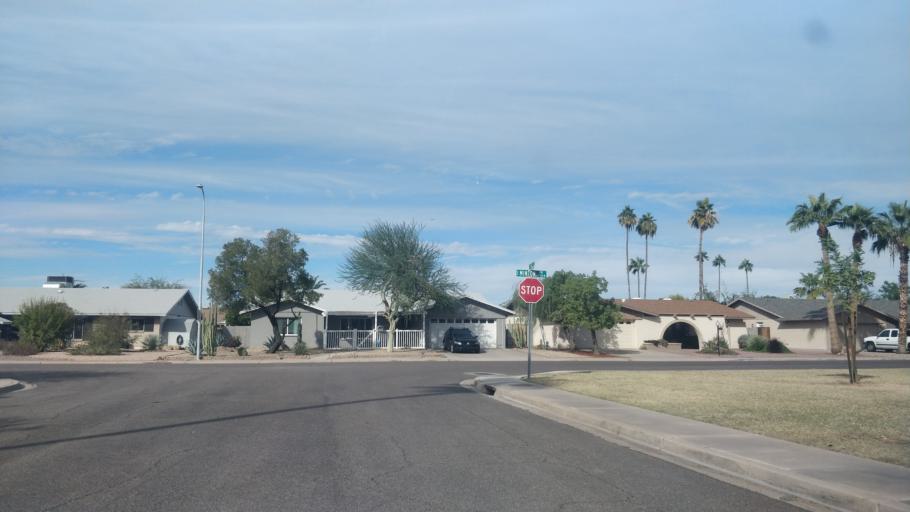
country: US
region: Arizona
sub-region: Maricopa County
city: Tempe
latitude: 33.3810
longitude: -111.9140
